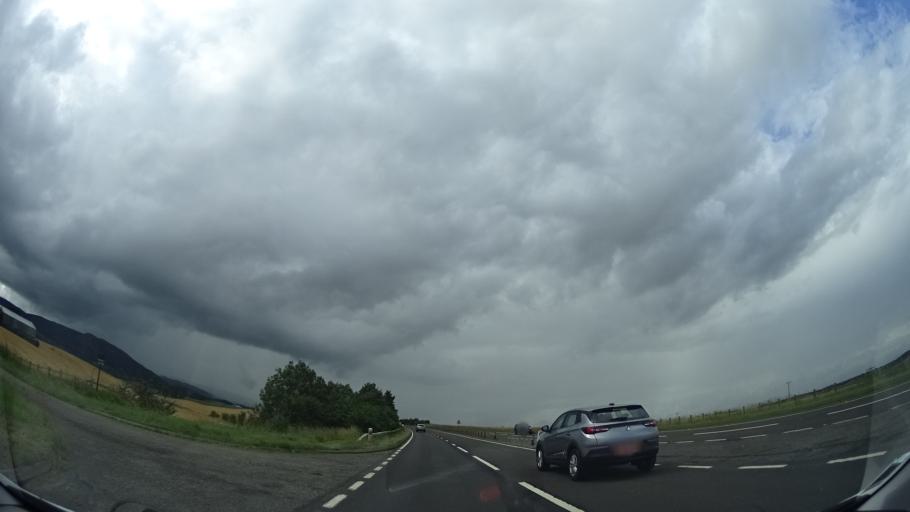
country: GB
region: Scotland
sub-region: Perth and Kinross
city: Auchterarder
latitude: 56.3311
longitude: -3.6335
